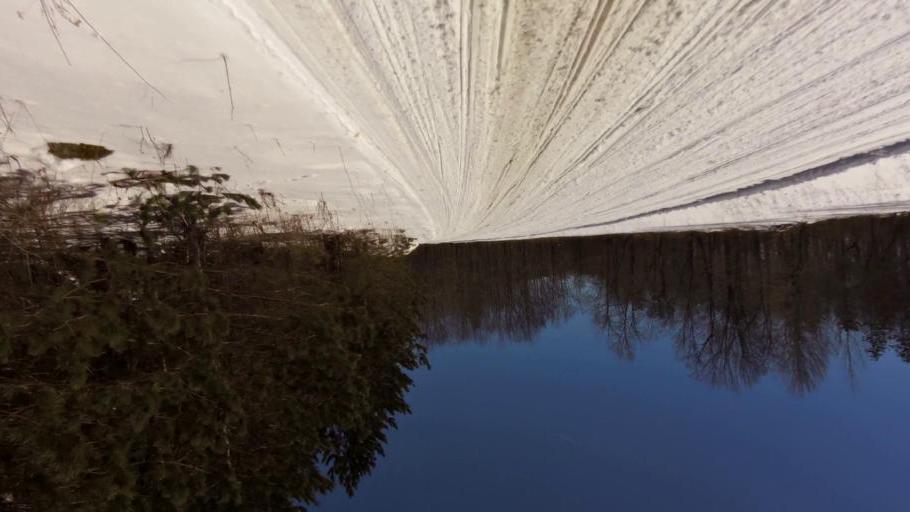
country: US
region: New York
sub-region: Allegany County
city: Houghton
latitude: 42.4004
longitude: -78.2674
